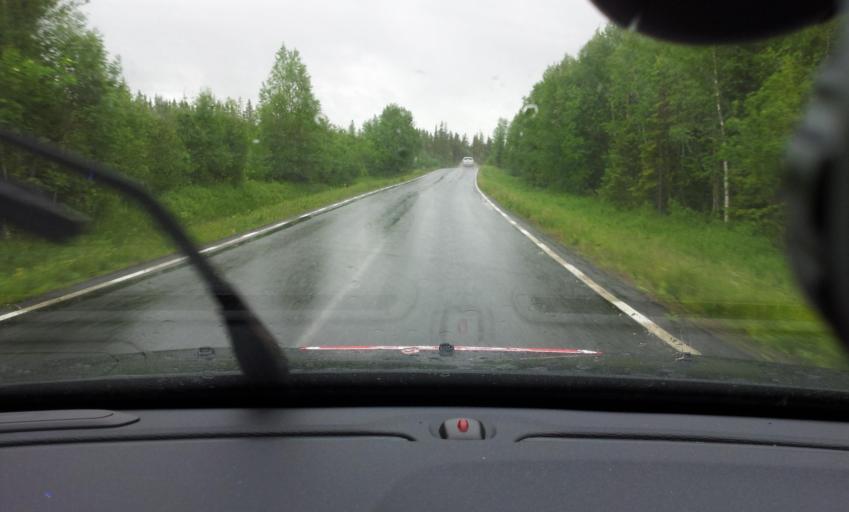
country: SE
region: Jaemtland
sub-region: Are Kommun
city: Are
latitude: 63.3146
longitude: 13.1485
